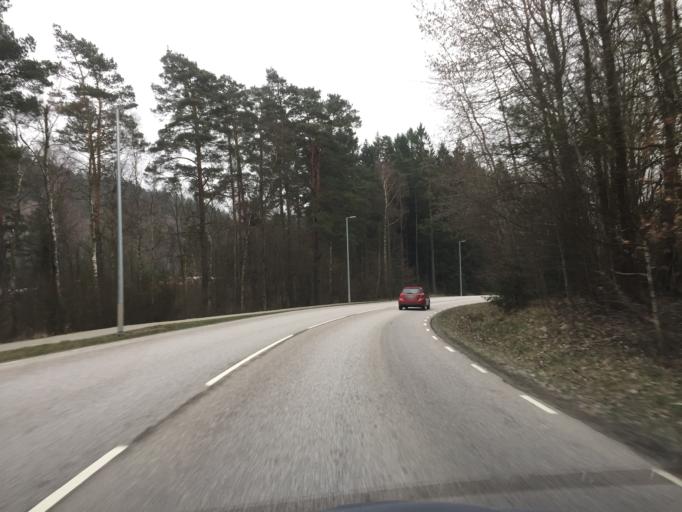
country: SE
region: Vaestra Goetaland
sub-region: Goteborg
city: Rannebergen
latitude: 57.7693
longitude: 12.0753
